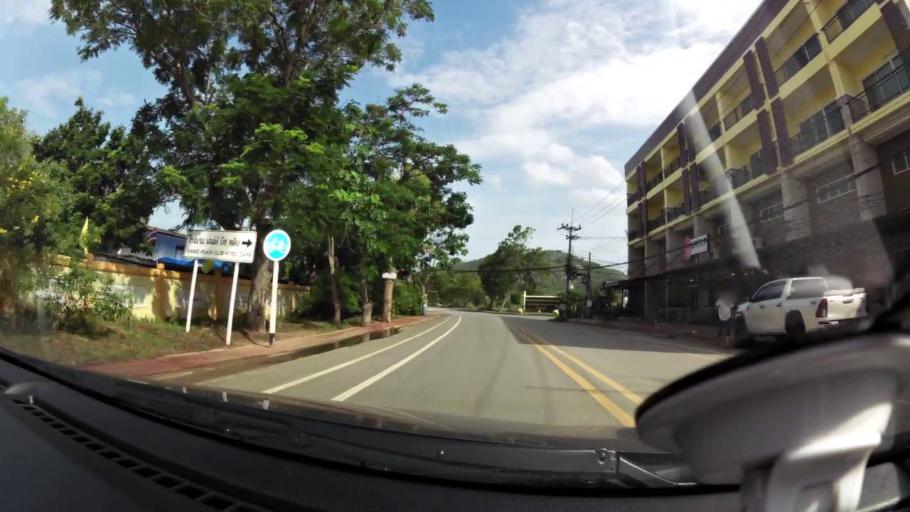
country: TH
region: Prachuap Khiri Khan
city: Pran Buri
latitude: 12.4618
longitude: 99.9746
